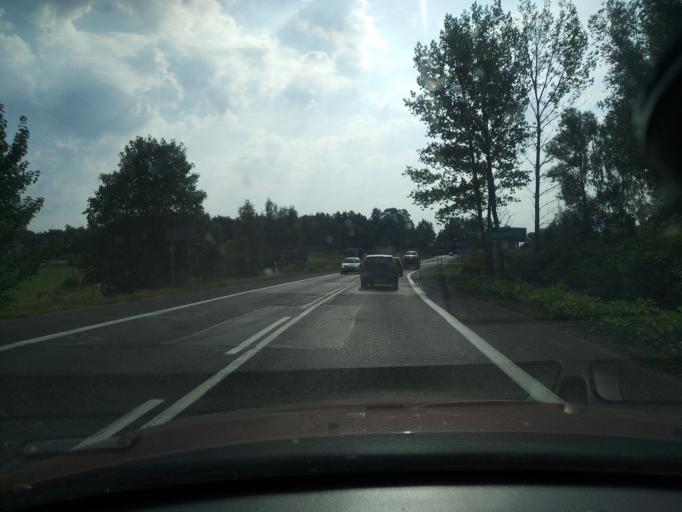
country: PL
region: Lower Silesian Voivodeship
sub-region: Powiat lwowecki
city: Gryfow Slaski
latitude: 51.0359
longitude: 15.4018
